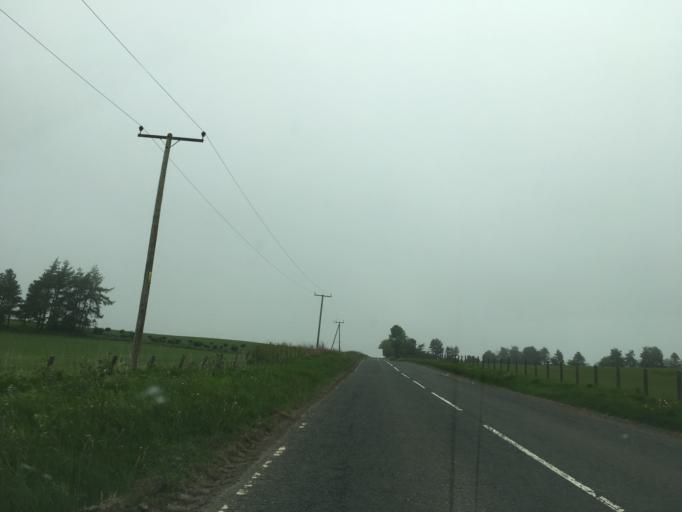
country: GB
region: Scotland
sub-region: The Scottish Borders
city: West Linton
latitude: 55.7417
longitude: -3.2968
